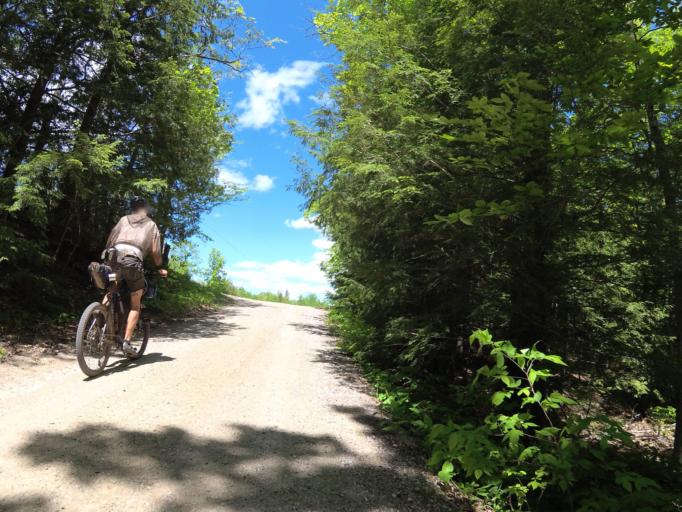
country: CA
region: Ontario
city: Renfrew
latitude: 45.0139
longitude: -76.8965
